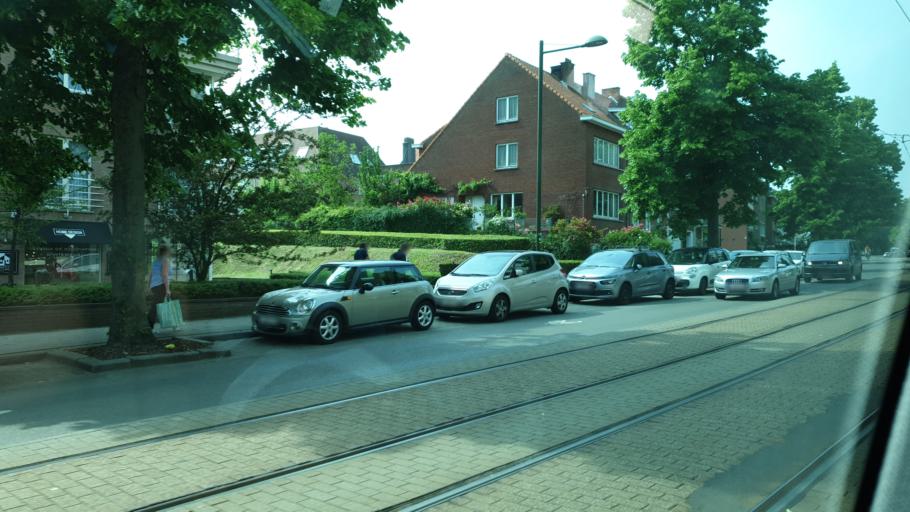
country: BE
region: Flanders
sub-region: Provincie Vlaams-Brabant
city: Kraainem
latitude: 50.8421
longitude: 4.4652
